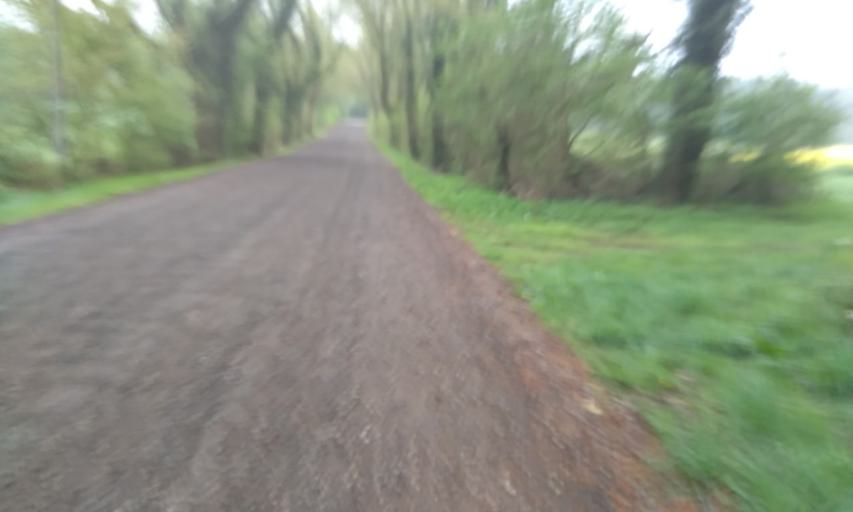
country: DE
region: Lower Saxony
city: Bliedersdorf
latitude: 53.4589
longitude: 9.5465
